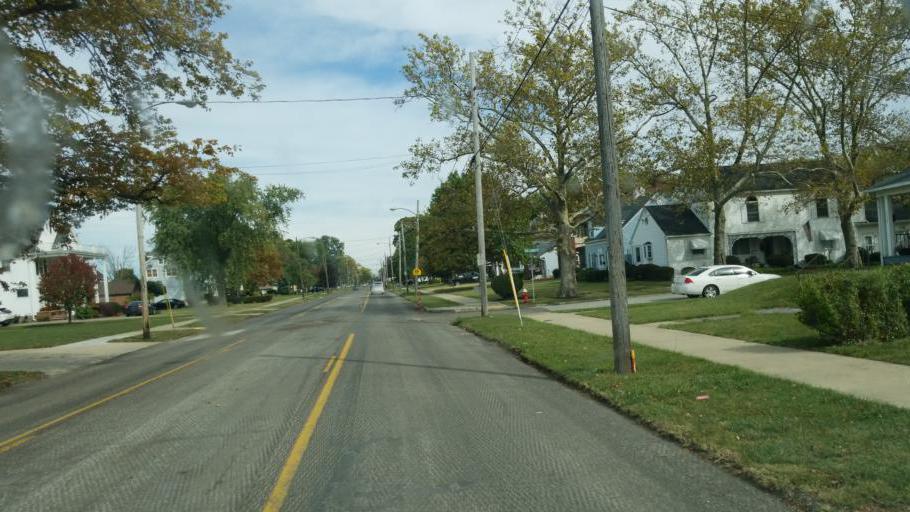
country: US
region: Ohio
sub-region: Lorain County
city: Lorain
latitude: 41.4760
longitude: -82.1570
